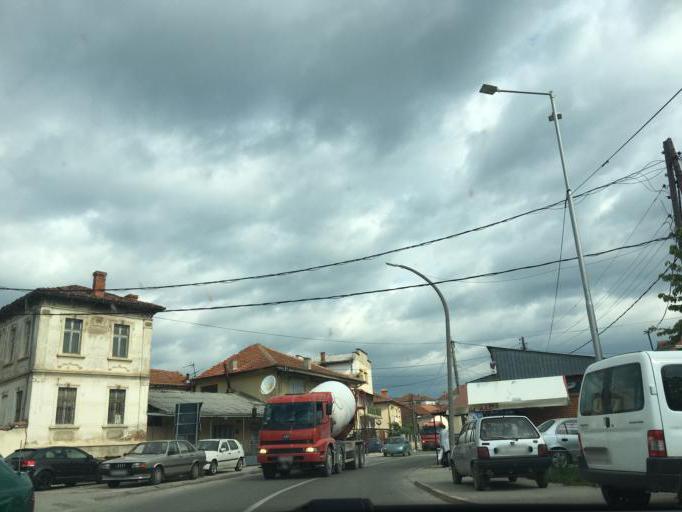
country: MK
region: Resen
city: Resen
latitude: 41.0928
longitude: 21.0115
